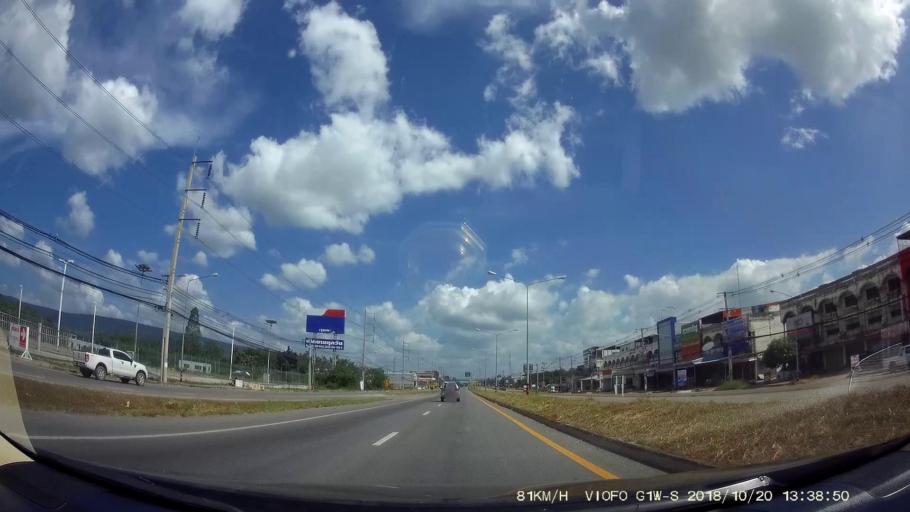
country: TH
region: Khon Kaen
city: Chum Phae
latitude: 16.5510
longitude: 102.0866
